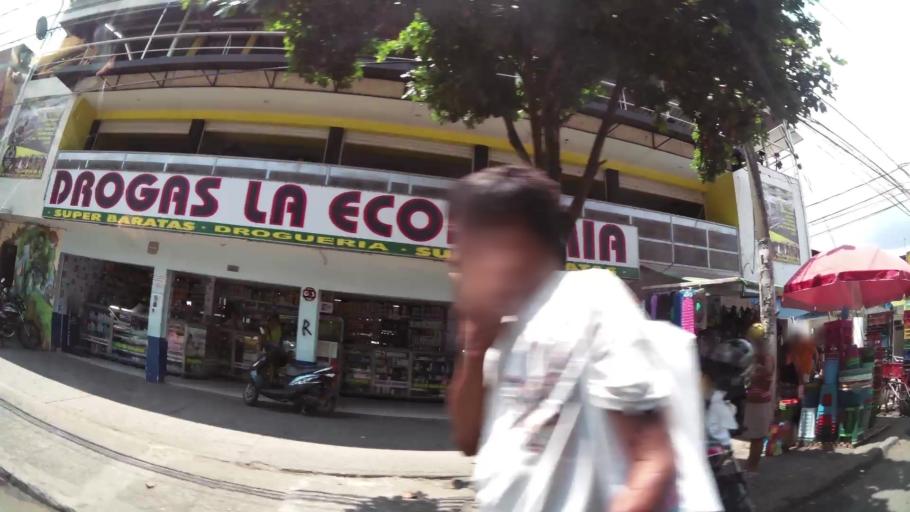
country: CO
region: Valle del Cauca
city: Cali
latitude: 3.4641
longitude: -76.4822
